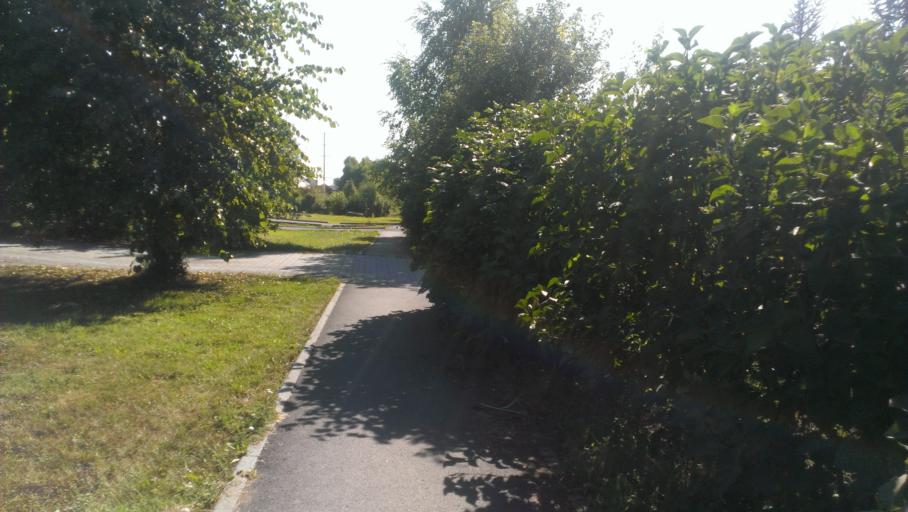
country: RU
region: Altai Krai
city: Novosilikatnyy
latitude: 53.3613
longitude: 83.6421
